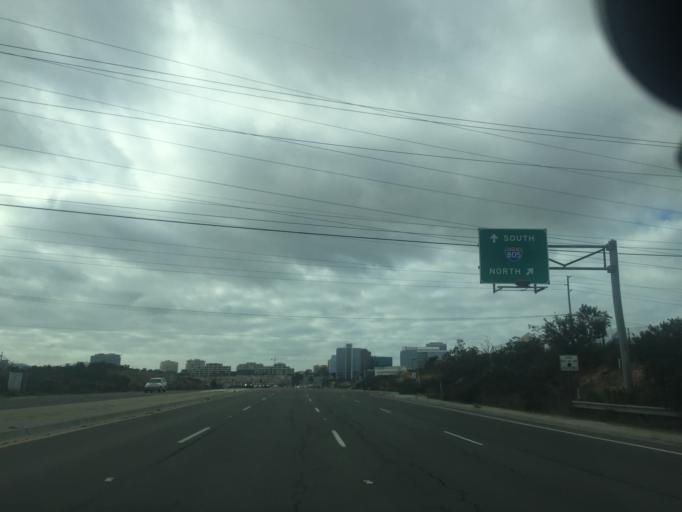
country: US
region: California
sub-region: San Diego County
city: La Jolla
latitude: 32.8761
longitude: -117.1940
